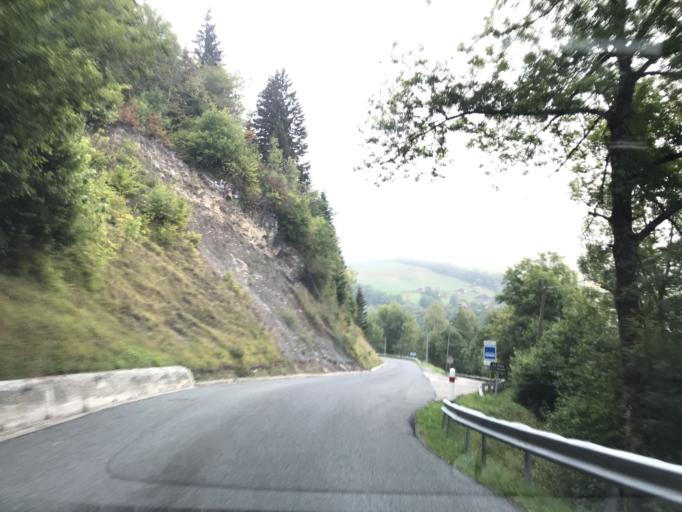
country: FR
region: Rhone-Alpes
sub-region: Departement de la Haute-Savoie
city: Doussard
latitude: 45.8065
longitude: 6.2548
